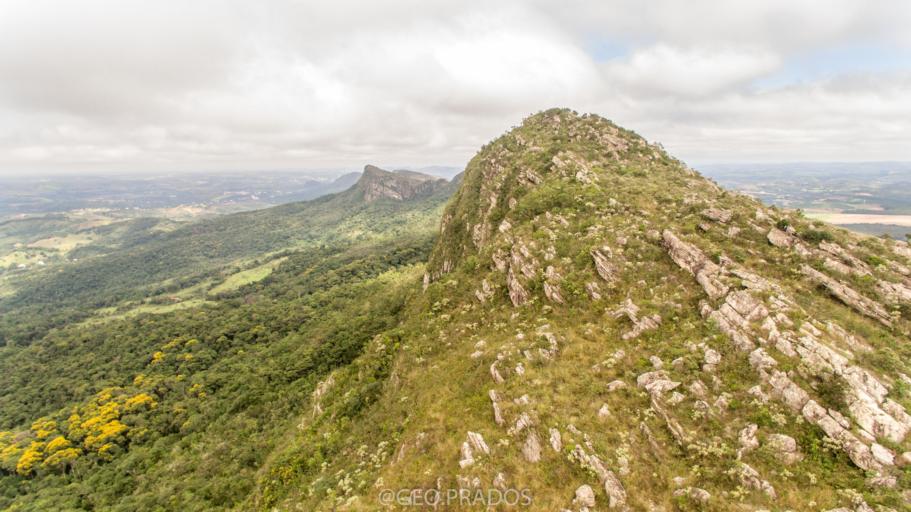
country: BR
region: Minas Gerais
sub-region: Tiradentes
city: Tiradentes
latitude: -21.0621
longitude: -44.1200
